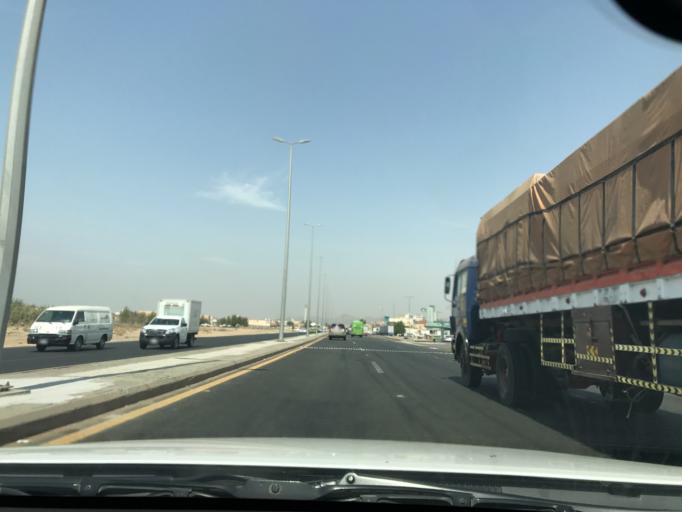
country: SA
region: Makkah
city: Jeddah
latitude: 21.3988
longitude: 39.4358
